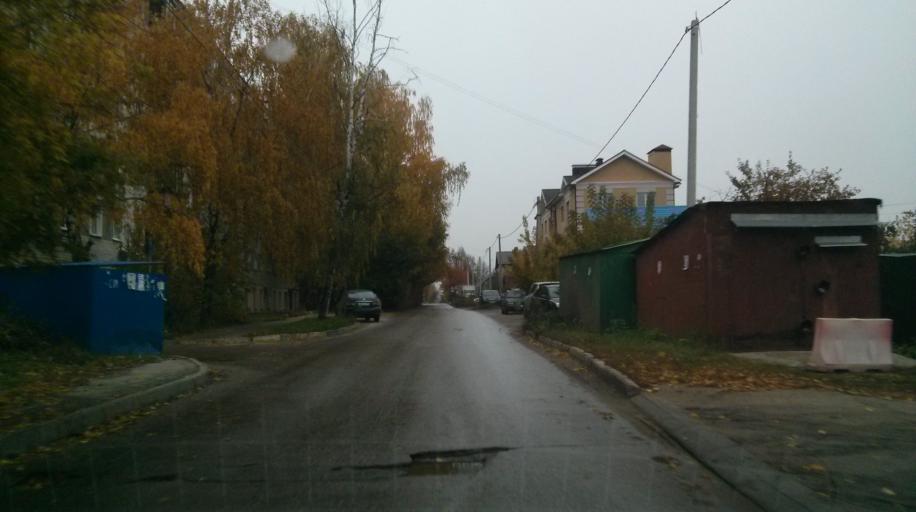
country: RU
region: Nizjnij Novgorod
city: Nizhniy Novgorod
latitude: 56.2920
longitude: 44.0200
